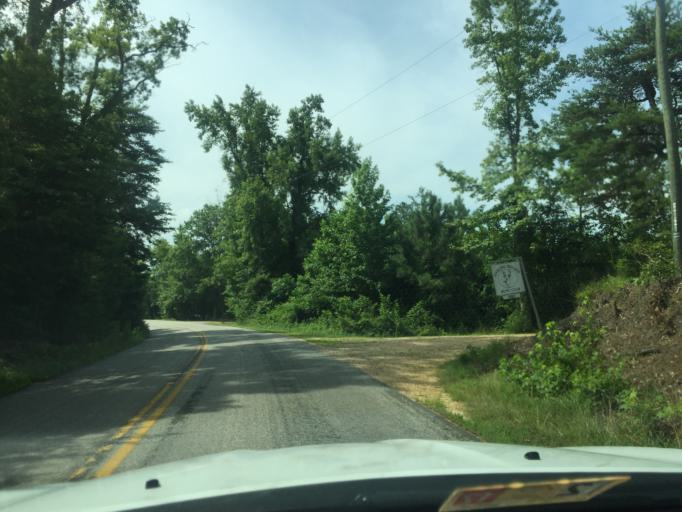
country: US
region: Virginia
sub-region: Charles City County
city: Charles City
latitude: 37.3905
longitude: -77.0153
